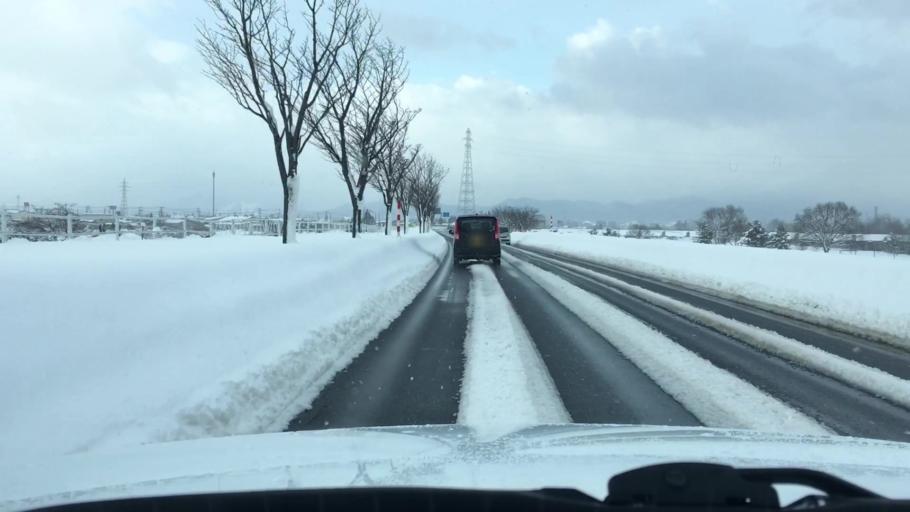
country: JP
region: Aomori
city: Hirosaki
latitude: 40.6319
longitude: 140.4730
